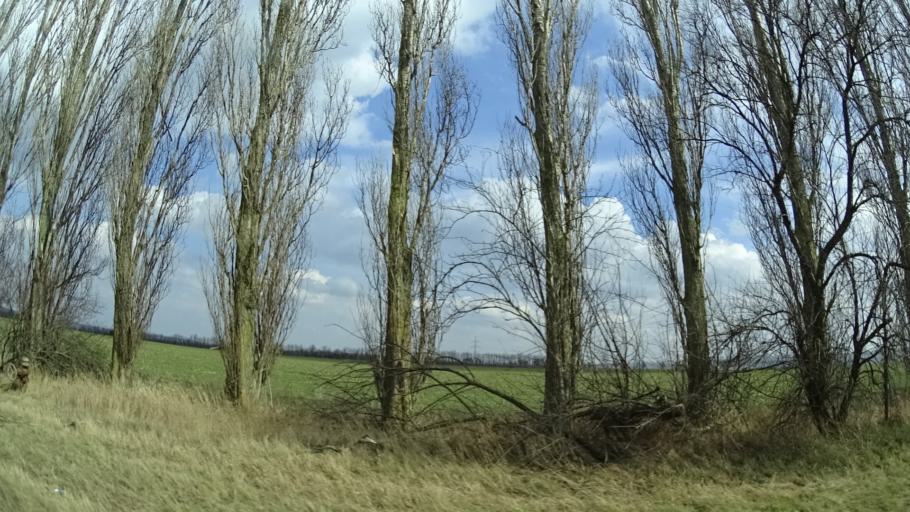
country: DE
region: Thuringia
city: Rannstedt
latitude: 51.0803
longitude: 11.5366
